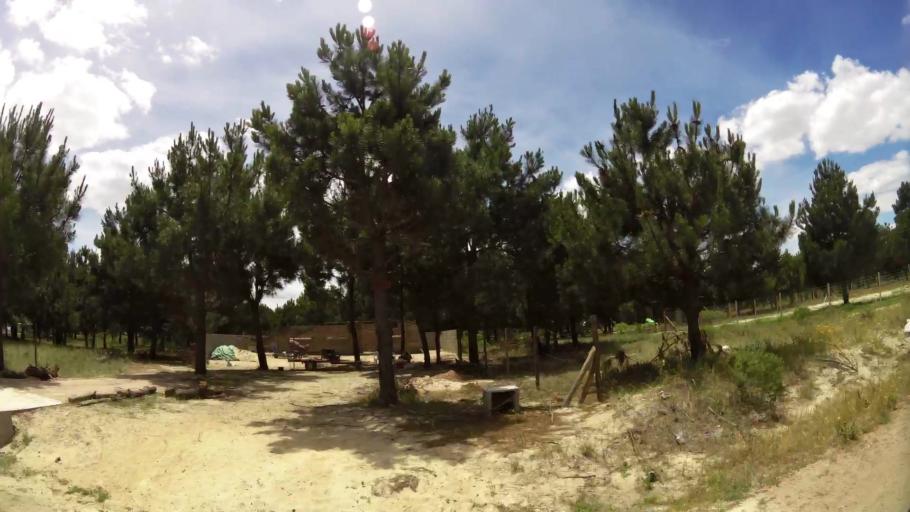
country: UY
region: Canelones
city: Pando
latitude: -34.8061
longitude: -55.9402
